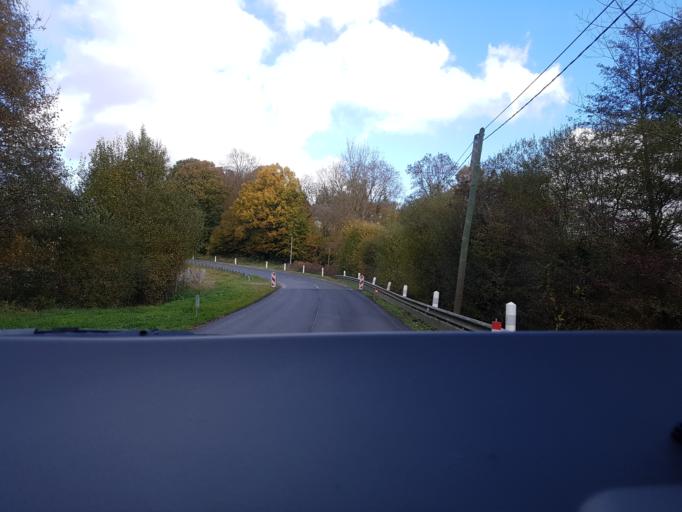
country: FR
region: Lower Normandy
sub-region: Departement de l'Orne
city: Champsecret
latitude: 48.6364
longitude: -0.5503
